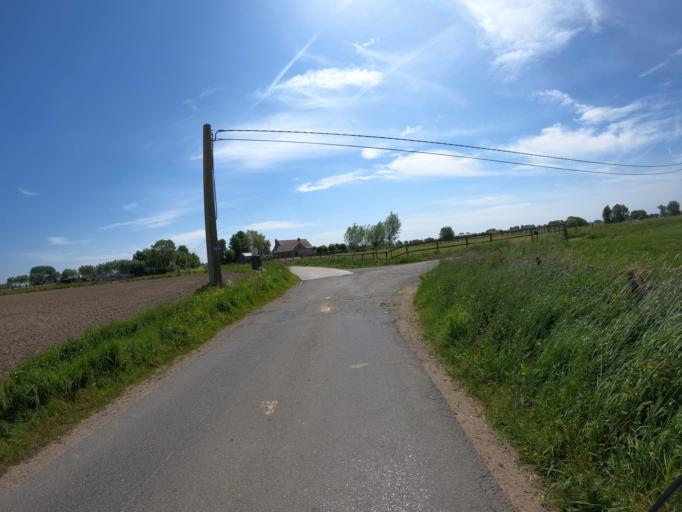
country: BE
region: Flanders
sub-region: Provincie West-Vlaanderen
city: Ruiselede
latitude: 51.0162
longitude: 3.4452
